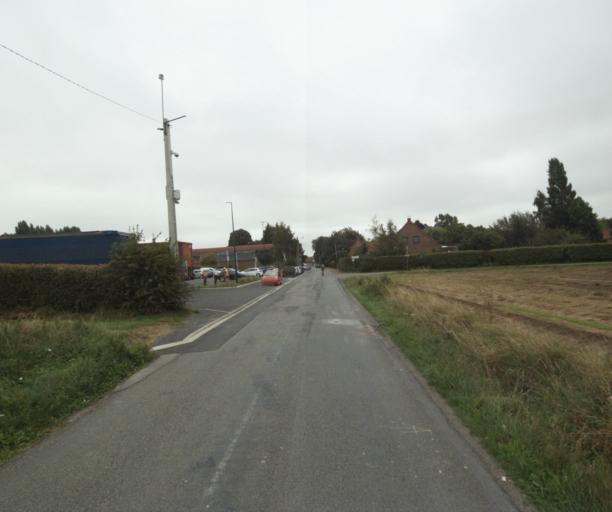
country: FR
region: Nord-Pas-de-Calais
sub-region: Departement du Nord
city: Willems
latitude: 50.6330
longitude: 3.2319
